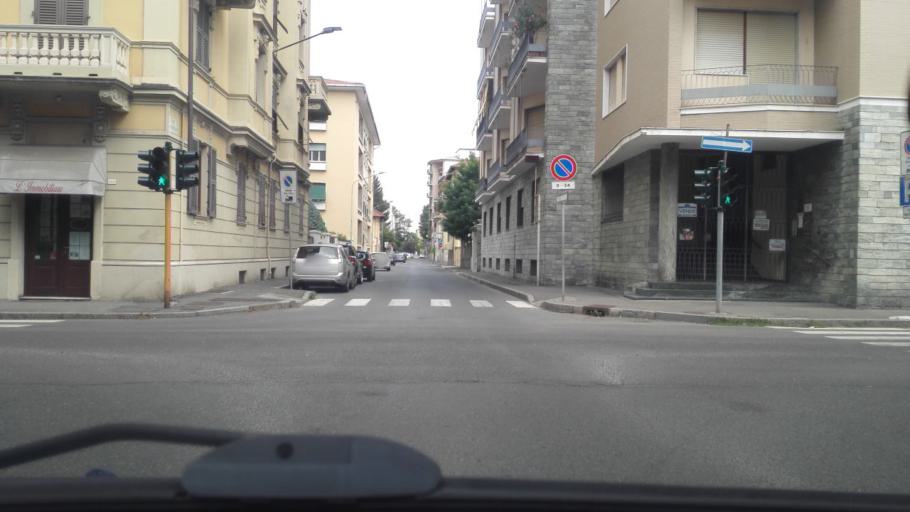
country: IT
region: Piedmont
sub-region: Provincia di Alessandria
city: Novi Ligure
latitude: 44.7650
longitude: 8.7896
